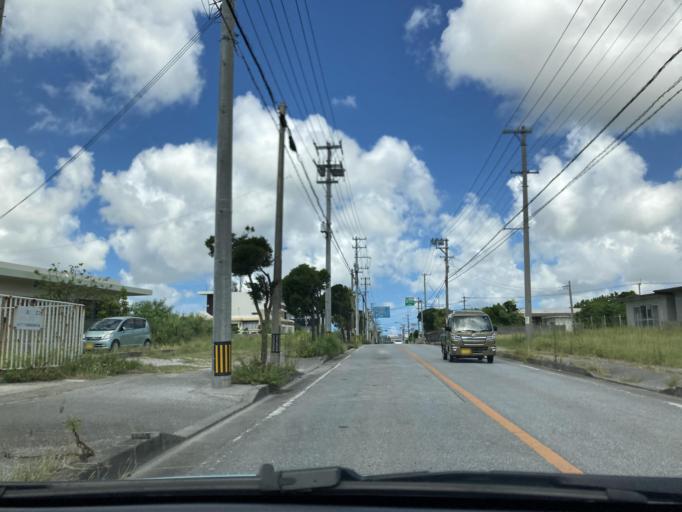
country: JP
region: Okinawa
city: Tomigusuku
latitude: 26.1465
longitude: 127.7255
